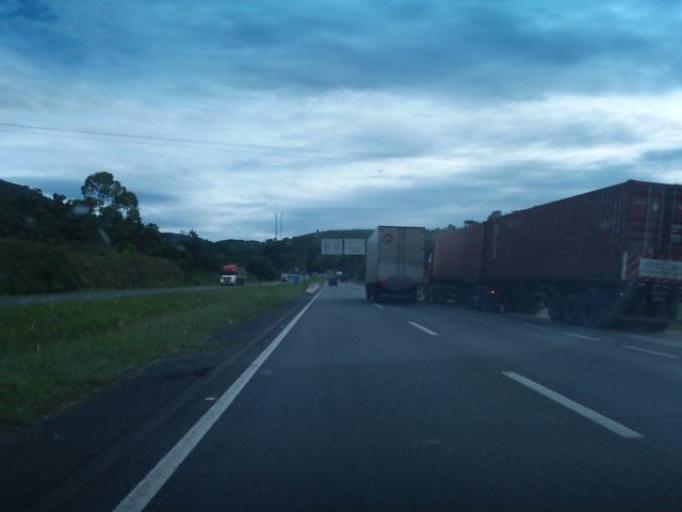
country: BR
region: Parana
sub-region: Campina Grande Do Sul
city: Campina Grande do Sul
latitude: -25.1232
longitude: -48.8561
